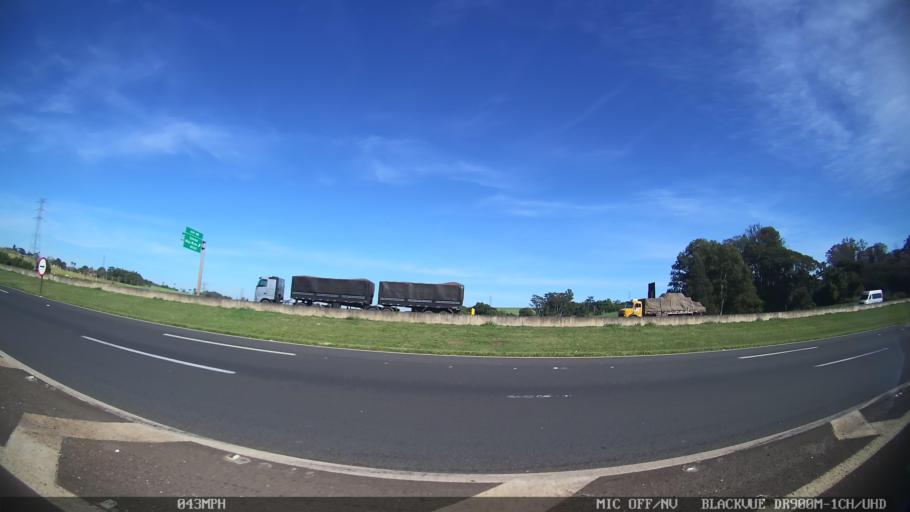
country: BR
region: Sao Paulo
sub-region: Araras
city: Araras
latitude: -22.3940
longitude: -47.3916
